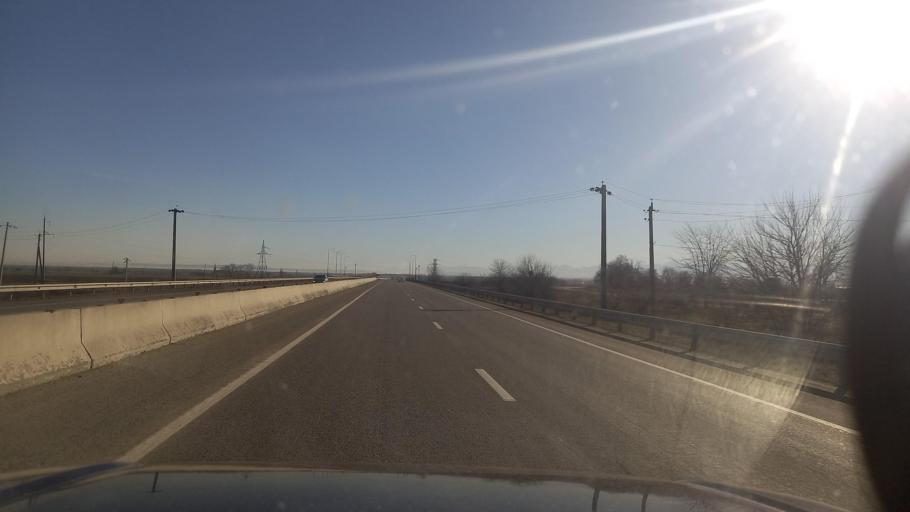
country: RU
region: Kabardino-Balkariya
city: Kishpek
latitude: 43.5893
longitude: 43.6775
